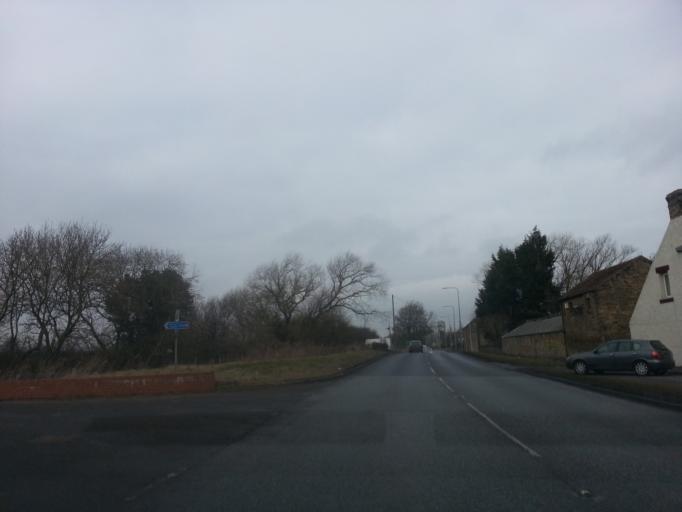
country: GB
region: England
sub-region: County Durham
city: High Etherley
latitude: 54.6232
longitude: -1.7096
